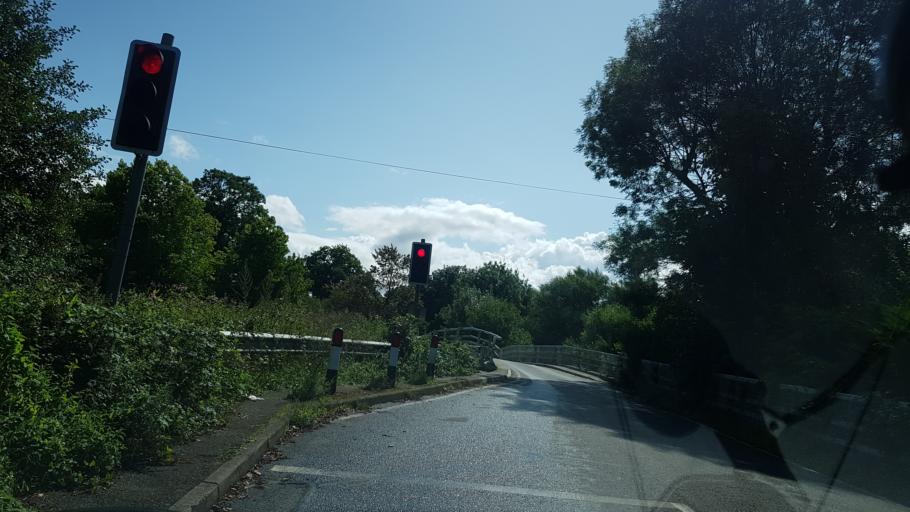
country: GB
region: England
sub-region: Surrey
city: Ripley
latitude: 51.3068
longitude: -0.5099
